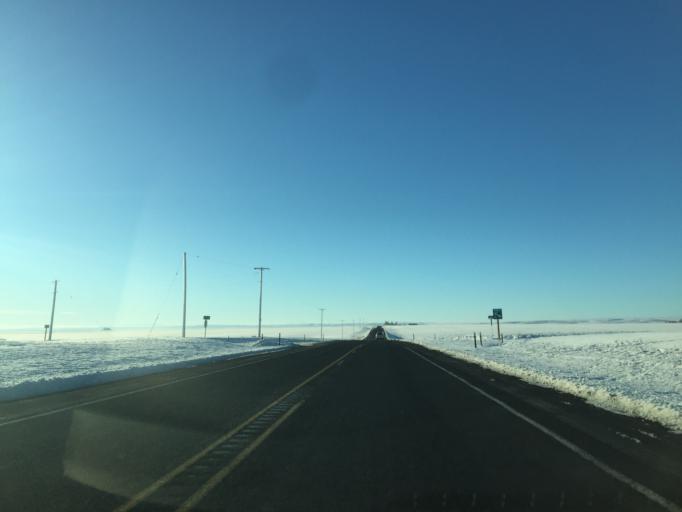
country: US
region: Washington
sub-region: Okanogan County
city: Coulee Dam
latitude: 47.6845
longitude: -118.9966
